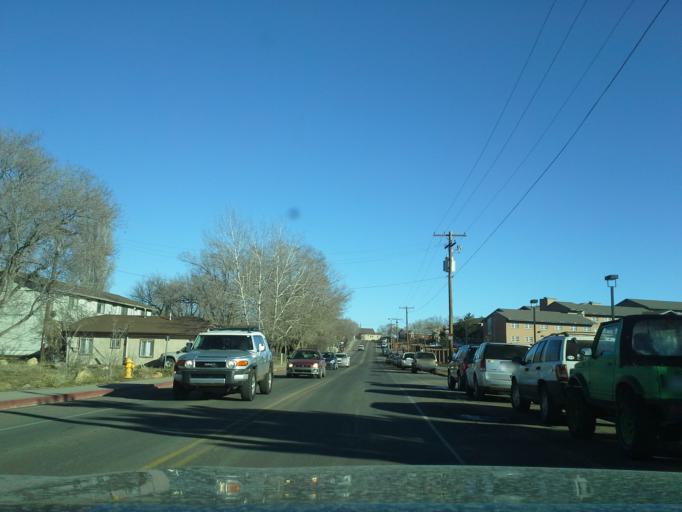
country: US
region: Arizona
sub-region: Coconino County
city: Flagstaff
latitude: 35.1908
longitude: -111.6510
